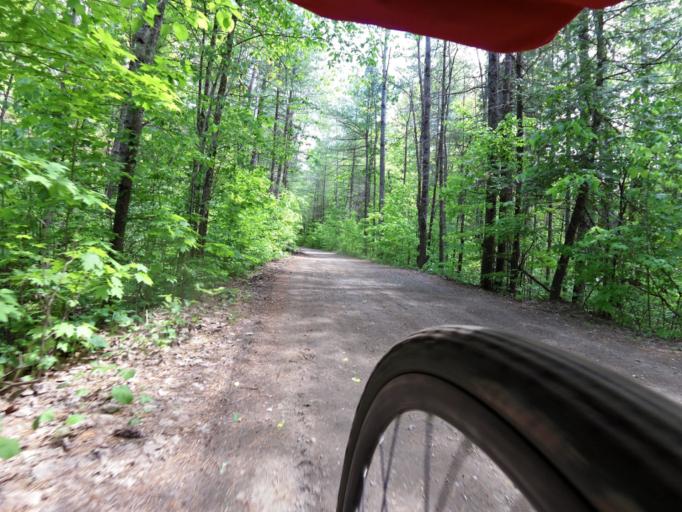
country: CA
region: Ontario
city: Renfrew
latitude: 45.2095
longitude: -76.6919
